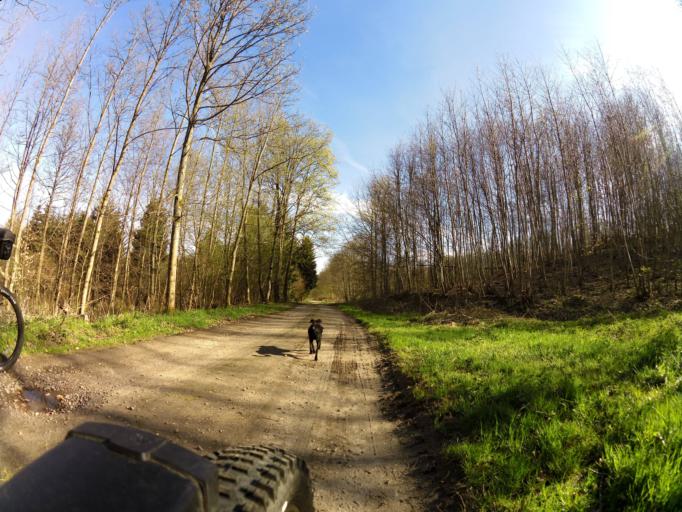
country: PL
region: West Pomeranian Voivodeship
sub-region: Powiat lobeski
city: Lobez
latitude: 53.7640
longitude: 15.5875
